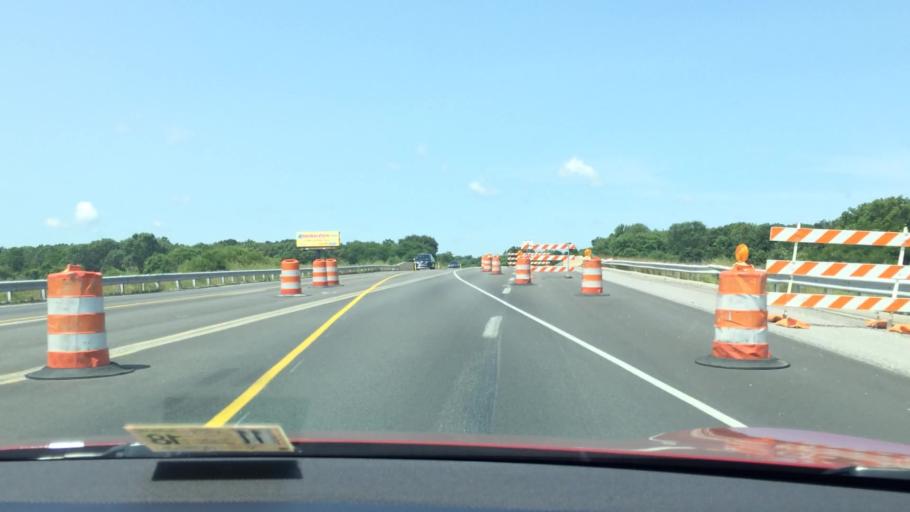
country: US
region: Indiana
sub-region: LaPorte County
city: Hudson Lake
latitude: 41.6703
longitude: -86.6147
